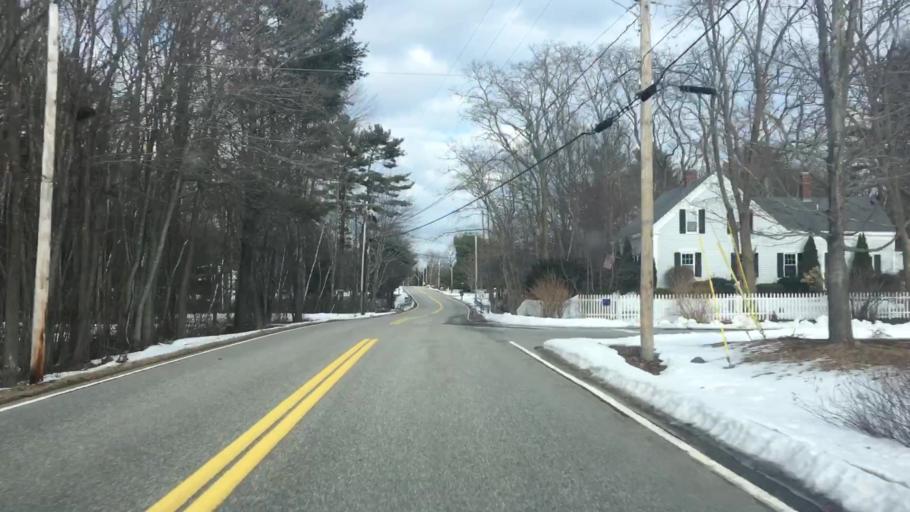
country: US
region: Maine
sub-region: York County
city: Biddeford
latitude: 43.4394
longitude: -70.4449
